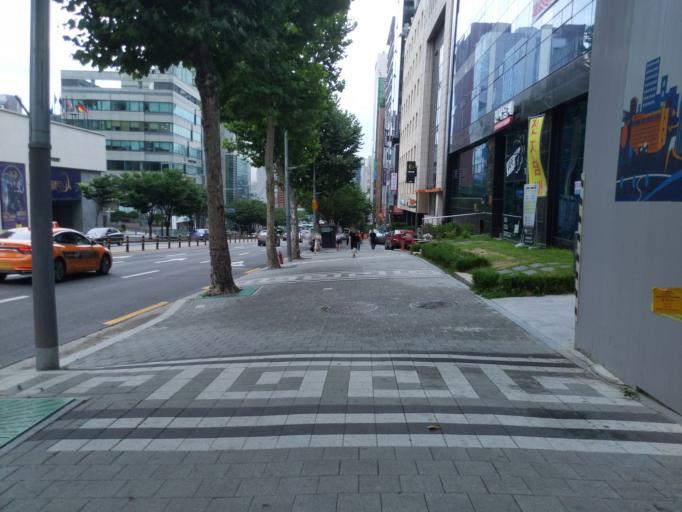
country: KR
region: Seoul
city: Seoul
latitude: 37.5055
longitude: 127.0274
